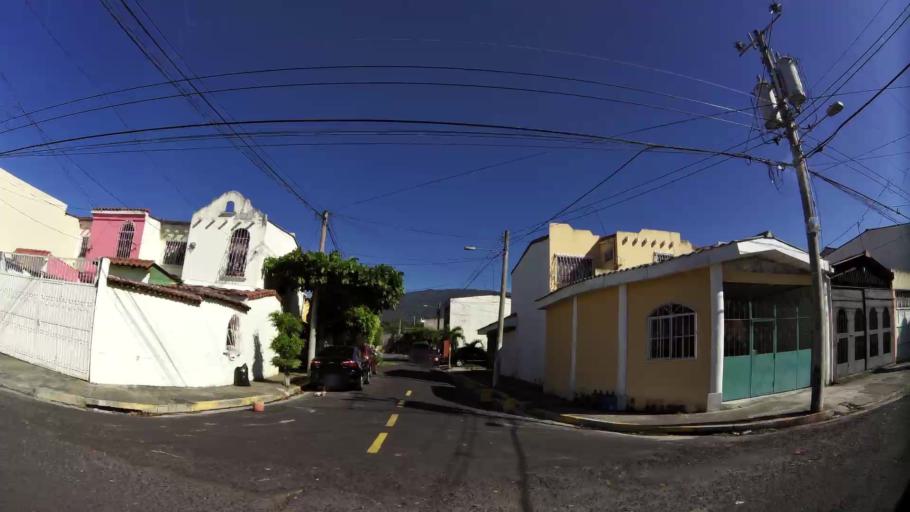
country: SV
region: La Libertad
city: Santa Tecla
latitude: 13.6812
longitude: -89.2973
